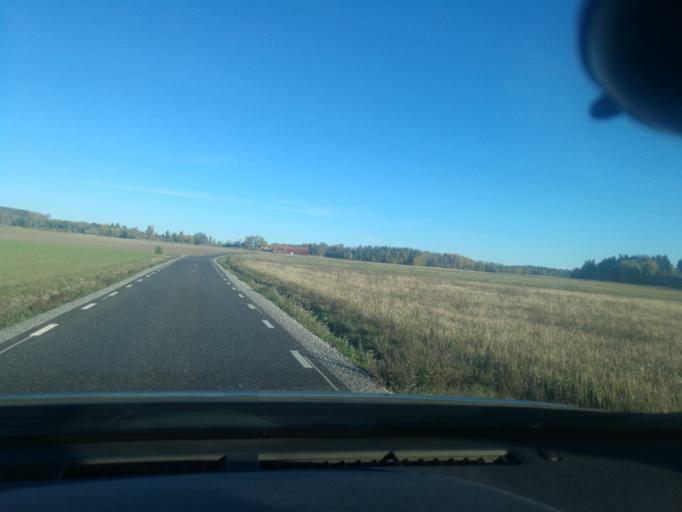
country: SE
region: Vaestmanland
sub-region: Kopings Kommun
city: Koping
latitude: 59.5658
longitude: 16.0512
